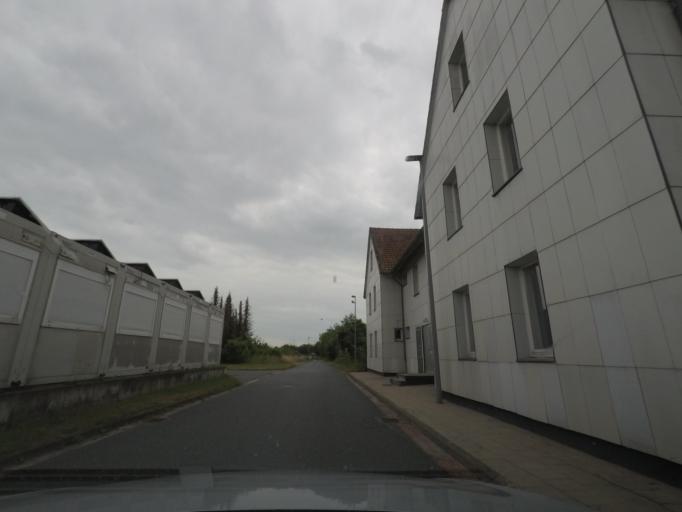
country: DE
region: Lower Saxony
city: Helmstedt
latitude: 52.2172
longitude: 11.0062
